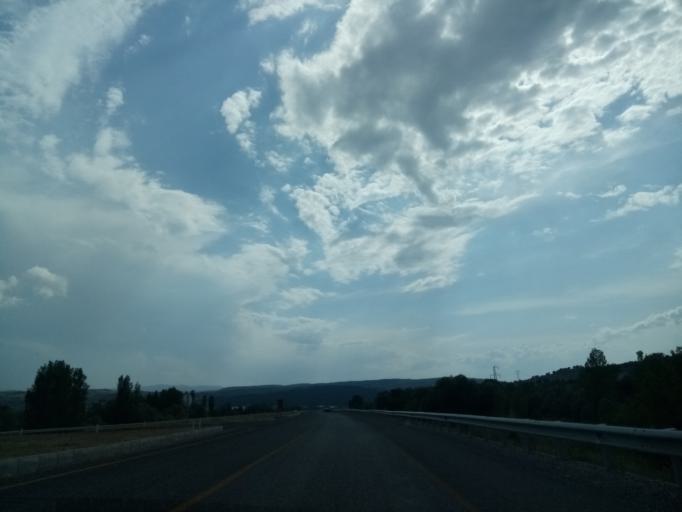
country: TR
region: Isparta
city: Bagkonak
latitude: 38.2024
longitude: 31.2600
